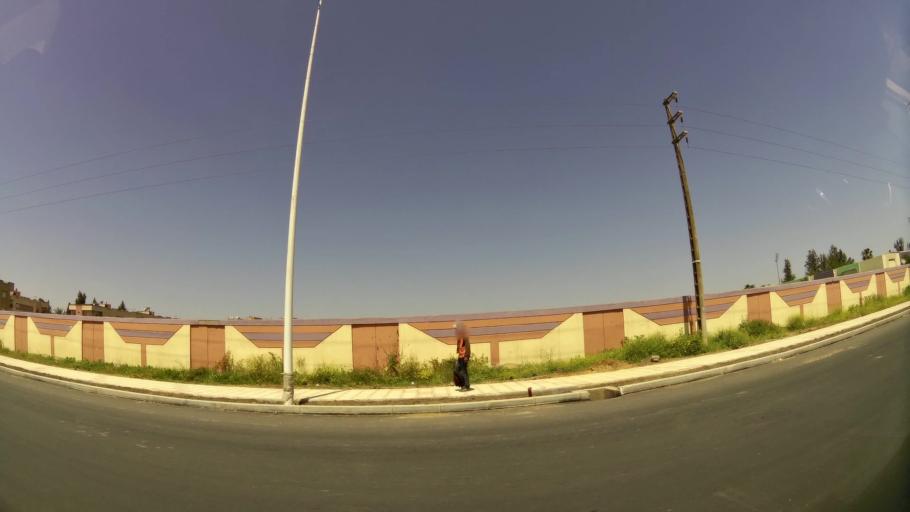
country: MA
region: Rabat-Sale-Zemmour-Zaer
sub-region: Khemisset
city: Khemisset
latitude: 33.8146
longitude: -6.0751
